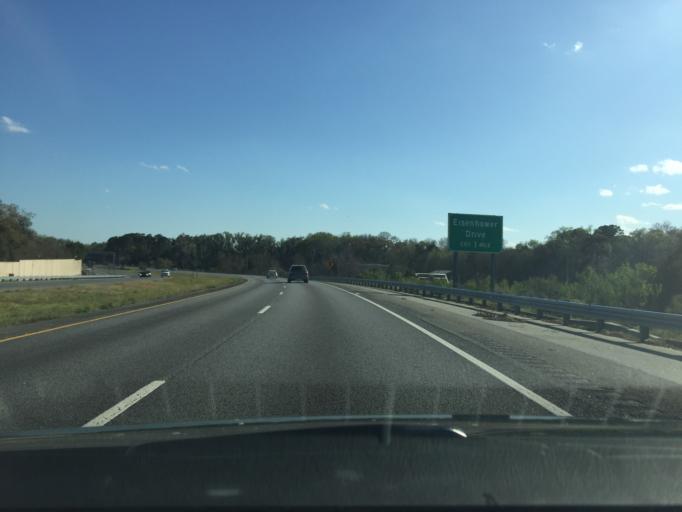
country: US
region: Georgia
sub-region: Chatham County
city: Thunderbolt
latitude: 32.0220
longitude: -81.0887
